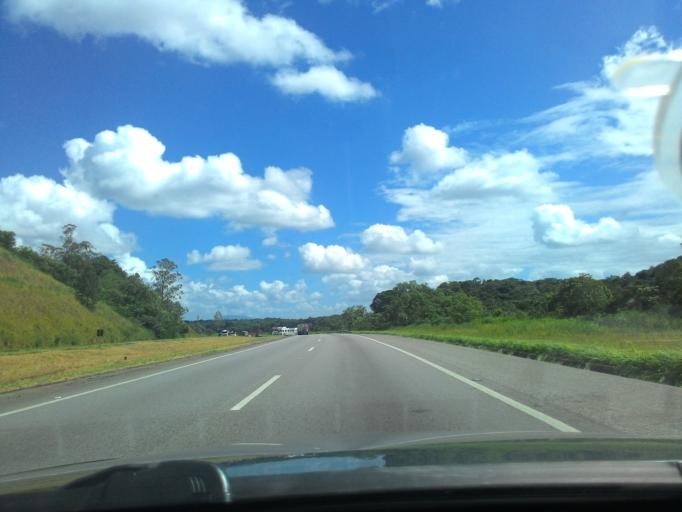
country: BR
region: Sao Paulo
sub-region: Registro
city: Registro
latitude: -24.5791
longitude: -47.8849
